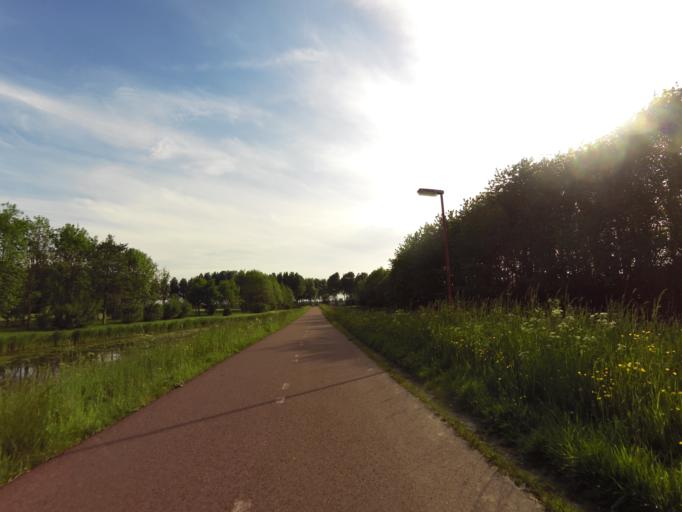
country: NL
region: South Holland
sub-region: Gemeente Pijnacker-Nootdorp
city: Pijnacker
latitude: 52.0544
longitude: 4.4319
